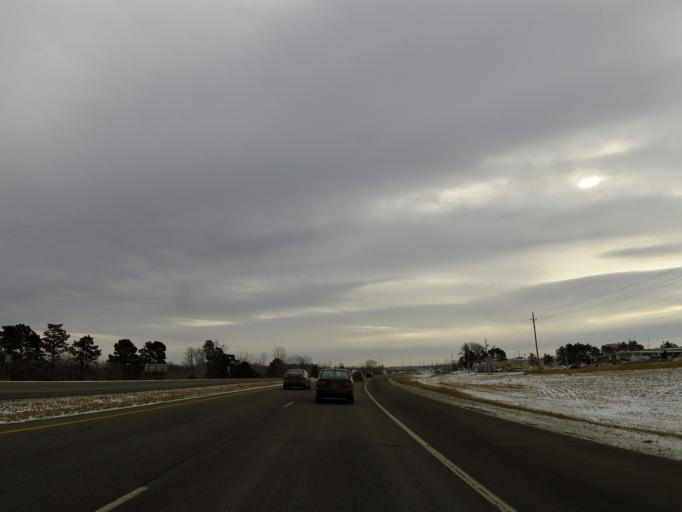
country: US
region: Minnesota
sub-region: Hennepin County
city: Eden Prairie
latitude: 44.7947
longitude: -93.4199
